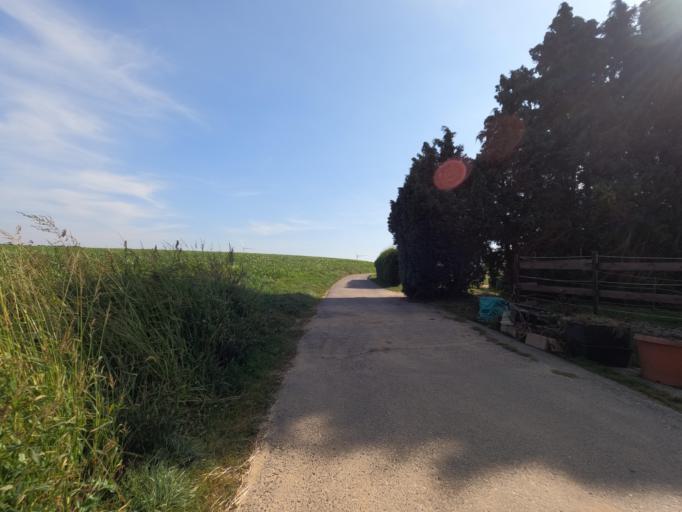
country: DE
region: North Rhine-Westphalia
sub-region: Regierungsbezirk Koln
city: Linnich
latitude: 50.9562
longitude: 6.2598
